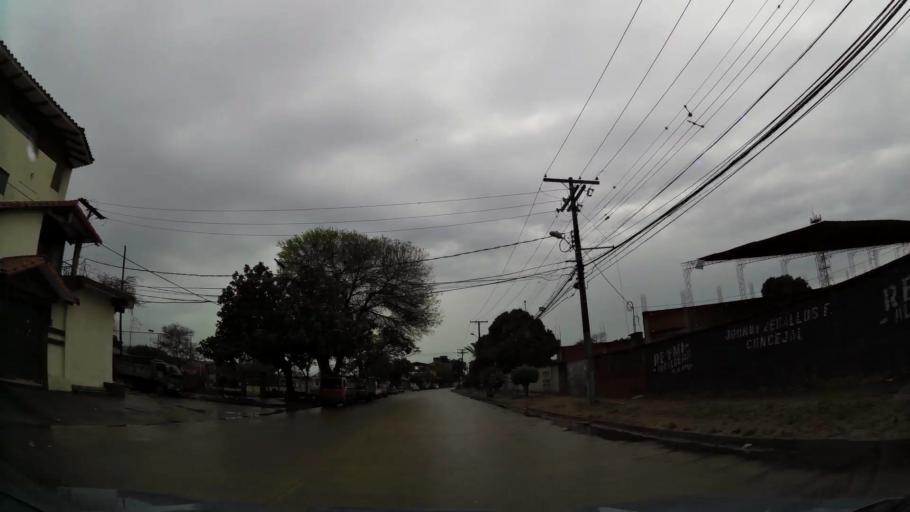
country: BO
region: Santa Cruz
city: Santa Cruz de la Sierra
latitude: -17.8128
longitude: -63.2063
